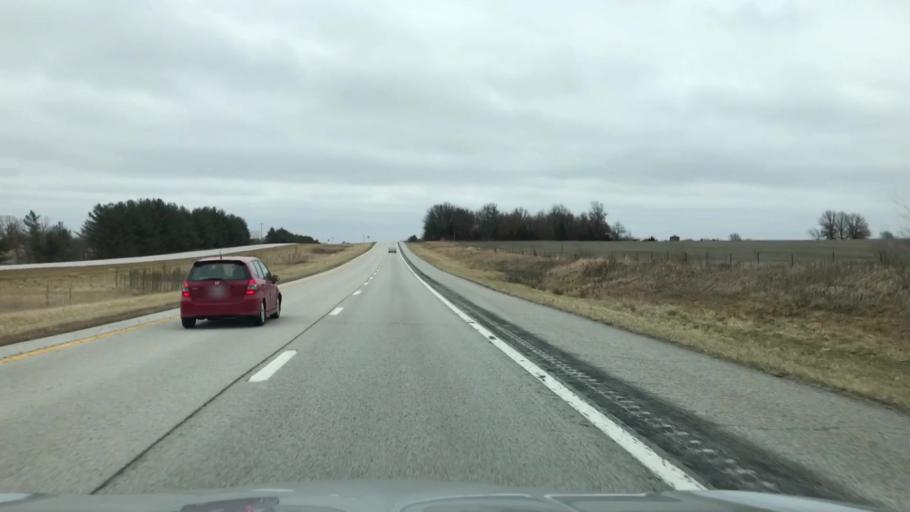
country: US
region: Missouri
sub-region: Livingston County
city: Chillicothe
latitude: 39.7771
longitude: -93.3732
